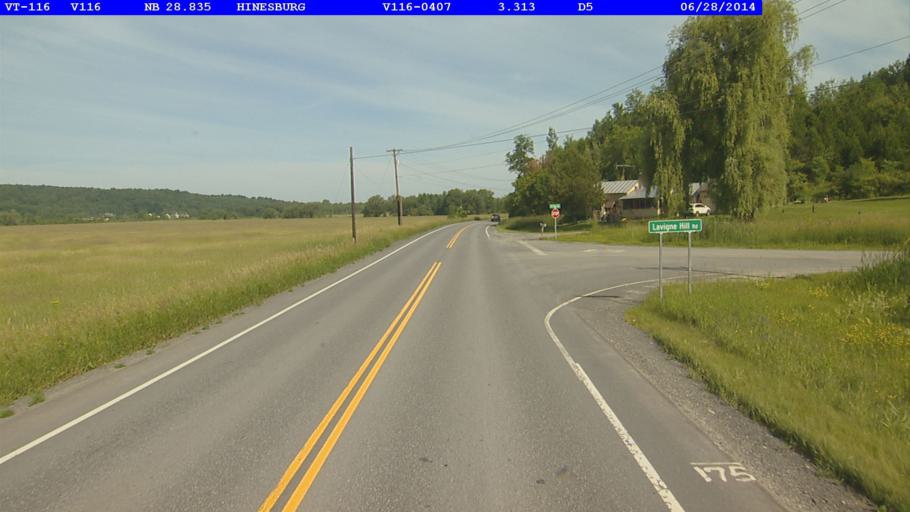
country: US
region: Vermont
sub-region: Chittenden County
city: Hinesburg
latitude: 44.3185
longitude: -73.0937
